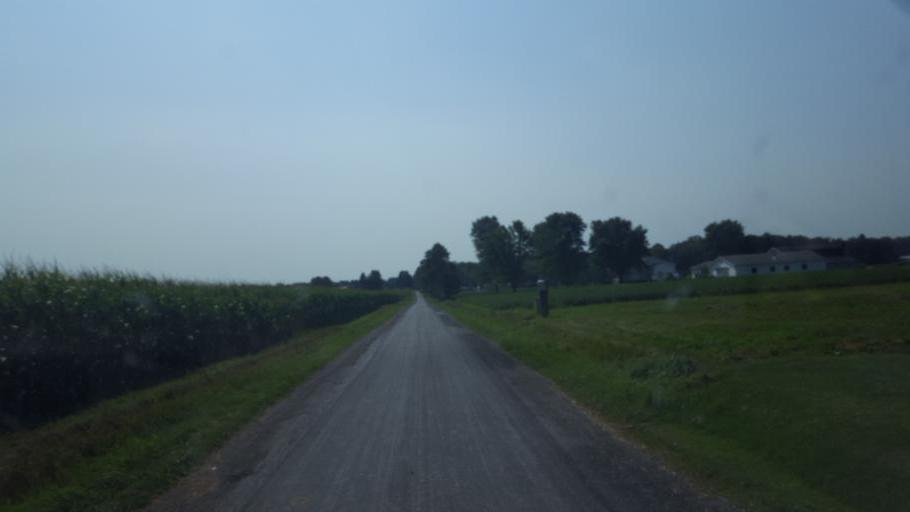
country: US
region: Ohio
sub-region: Ashtabula County
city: Orwell
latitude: 41.4996
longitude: -80.8777
